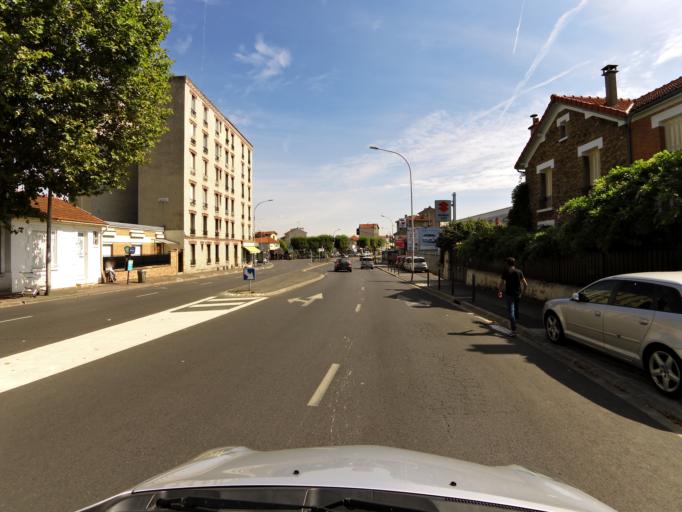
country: FR
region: Ile-de-France
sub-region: Departement du Val-de-Marne
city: Le Perreux-sur-Marne
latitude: 48.8486
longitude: 2.4949
